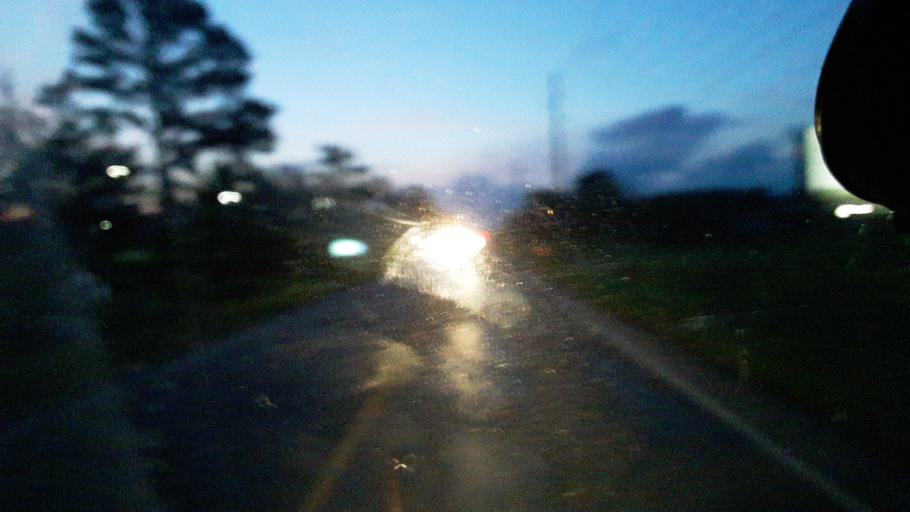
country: US
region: North Carolina
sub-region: Brunswick County
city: Oak Island
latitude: 33.9990
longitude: -78.2435
